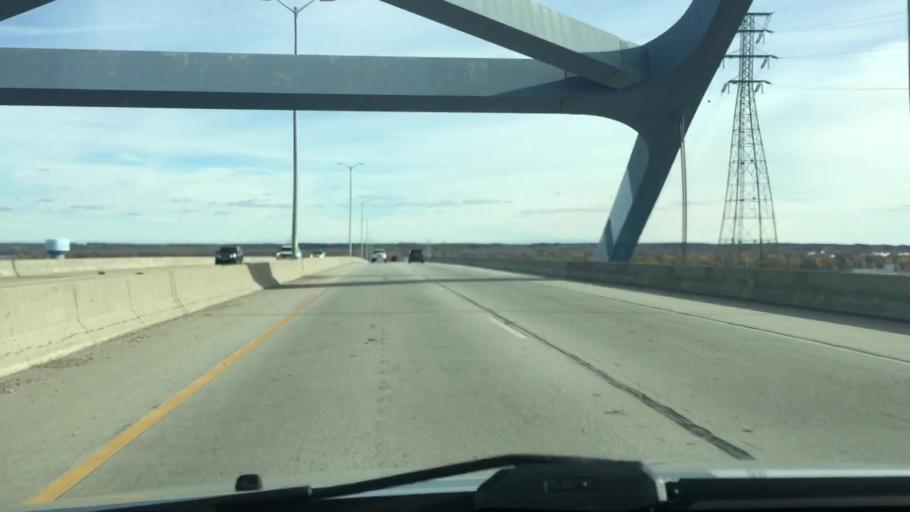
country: US
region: Wisconsin
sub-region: Brown County
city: Green Bay
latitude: 44.5332
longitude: -88.0074
